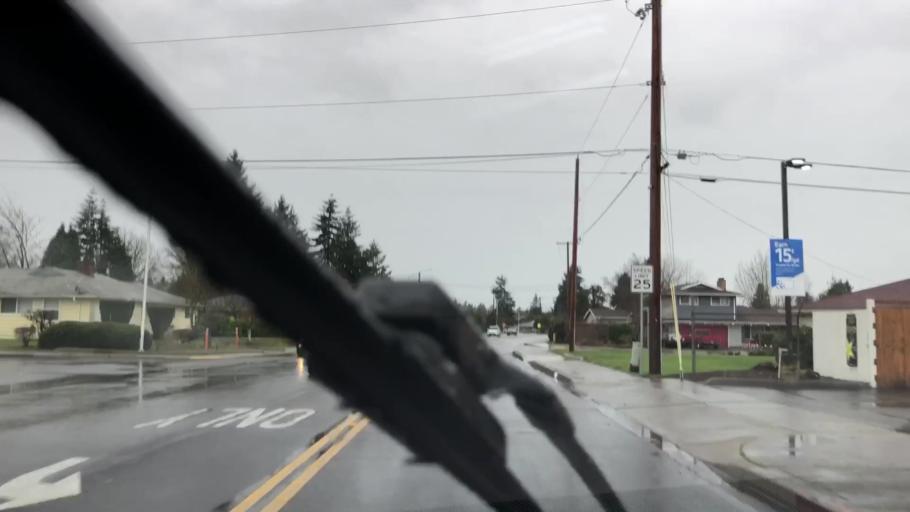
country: US
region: Washington
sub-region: Pierce County
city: Lakewood
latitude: 47.1595
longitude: -122.5053
